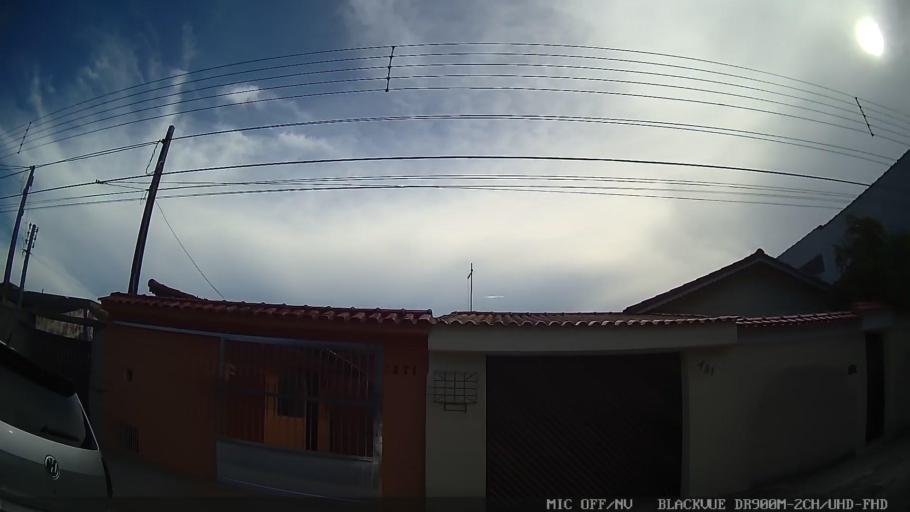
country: BR
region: Sao Paulo
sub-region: Iguape
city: Iguape
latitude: -24.7009
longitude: -47.5585
